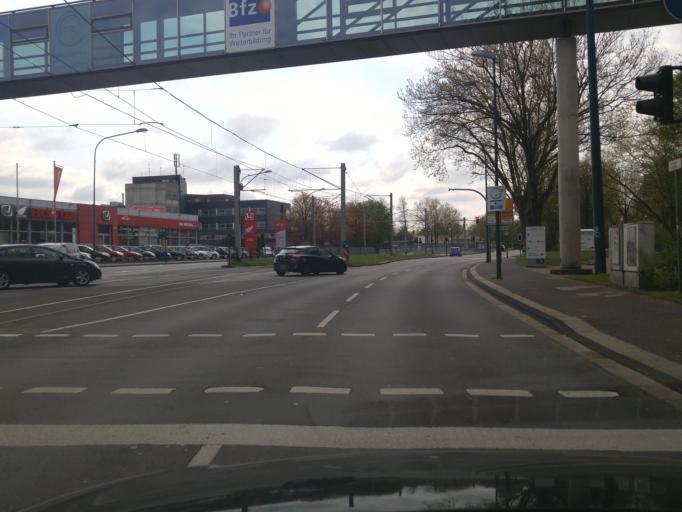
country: DE
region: North Rhine-Westphalia
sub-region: Regierungsbezirk Dusseldorf
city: Essen
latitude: 51.4716
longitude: 7.0170
